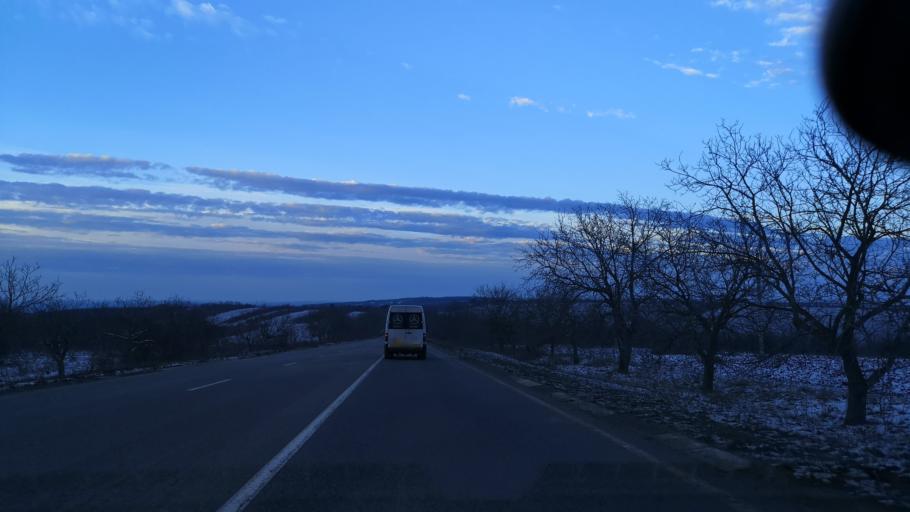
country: MD
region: Orhei
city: Orhei
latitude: 47.5398
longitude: 28.7931
